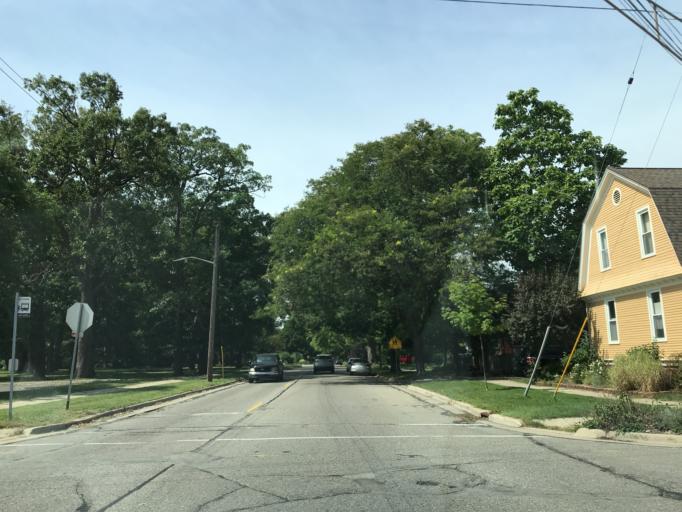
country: US
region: Michigan
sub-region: Washtenaw County
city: Ypsilanti
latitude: 42.2410
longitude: -83.6288
